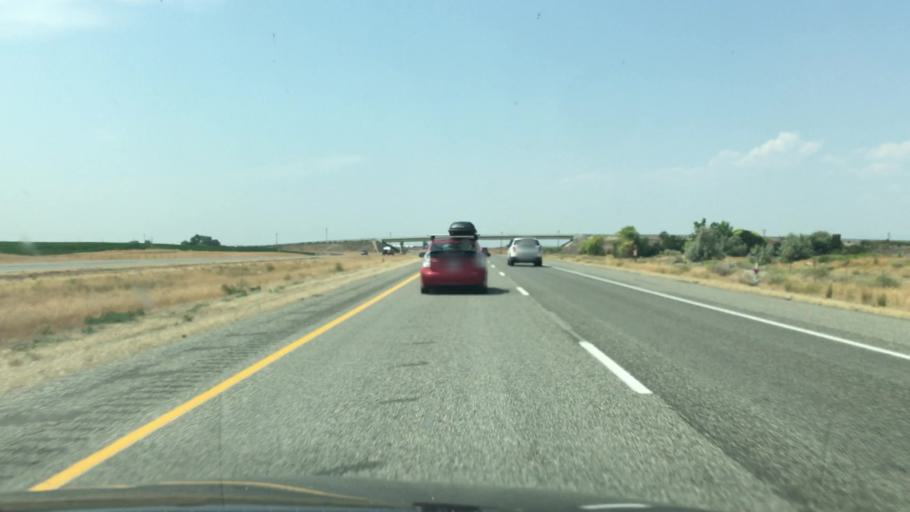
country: US
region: Idaho
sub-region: Gooding County
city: Wendell
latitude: 42.7941
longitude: -114.7502
